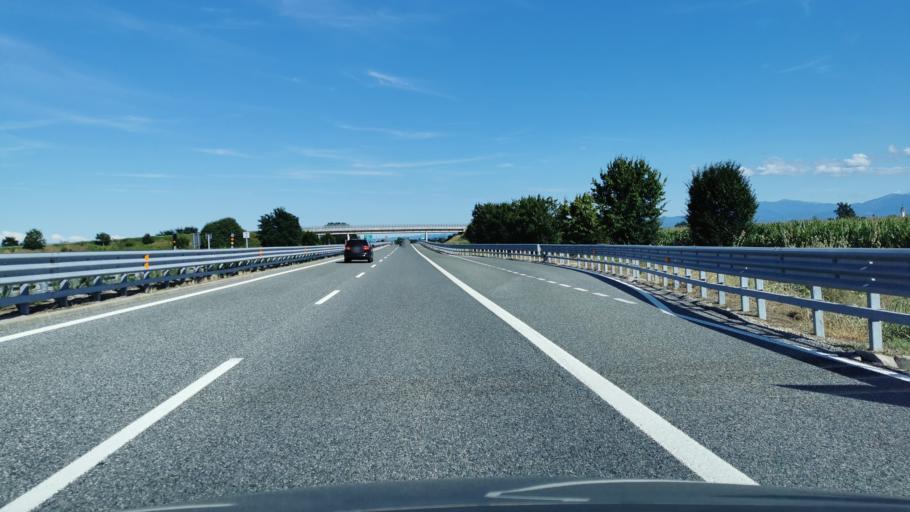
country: IT
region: Piedmont
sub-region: Provincia di Cuneo
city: Sant'Albano Stura
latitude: 44.4726
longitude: 7.7045
